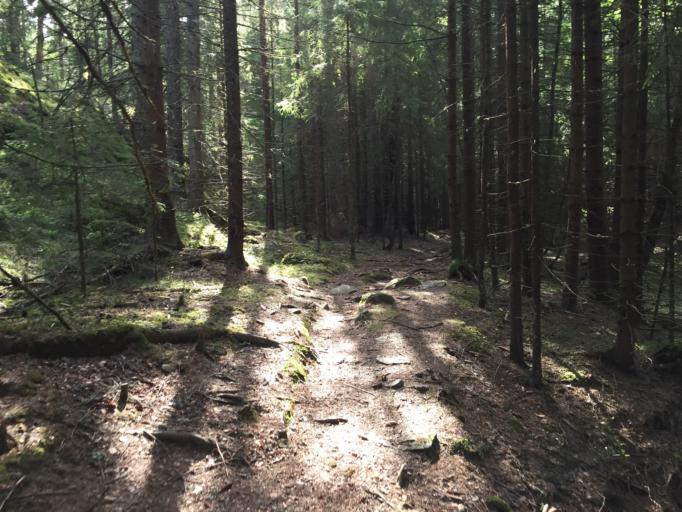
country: NO
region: Akershus
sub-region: Skedsmo
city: Lillestrom
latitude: 59.9241
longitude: 11.0134
